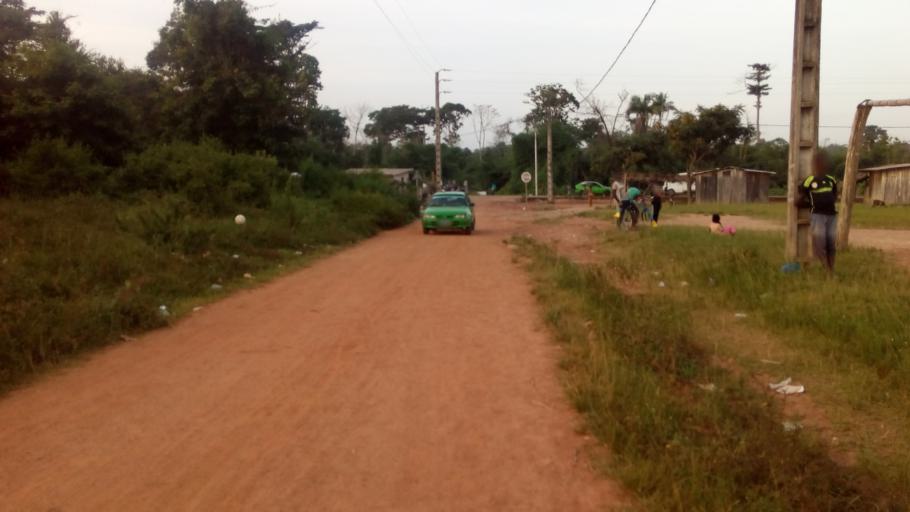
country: CI
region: Dix-Huit Montagnes
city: Duekoue
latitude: 6.7522
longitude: -7.3724
